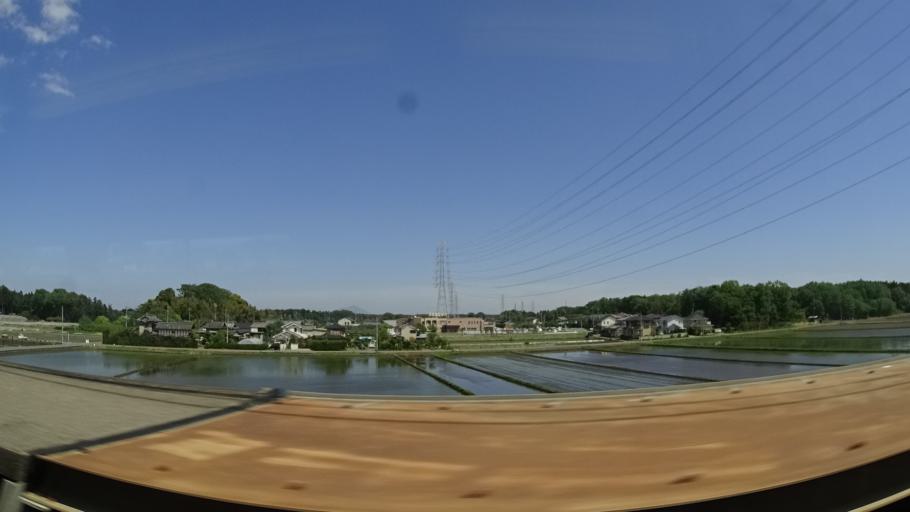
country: JP
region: Tochigi
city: Oyama
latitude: 36.2468
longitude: 139.7654
